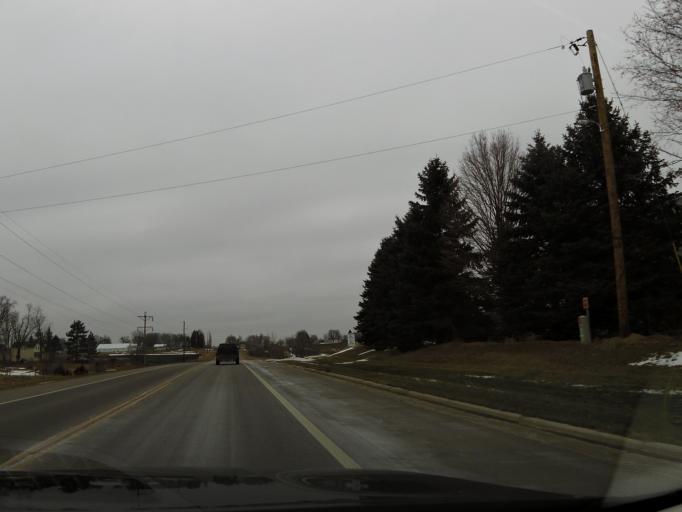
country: US
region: Minnesota
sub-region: Carver County
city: Waconia
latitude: 44.8963
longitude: -93.8185
